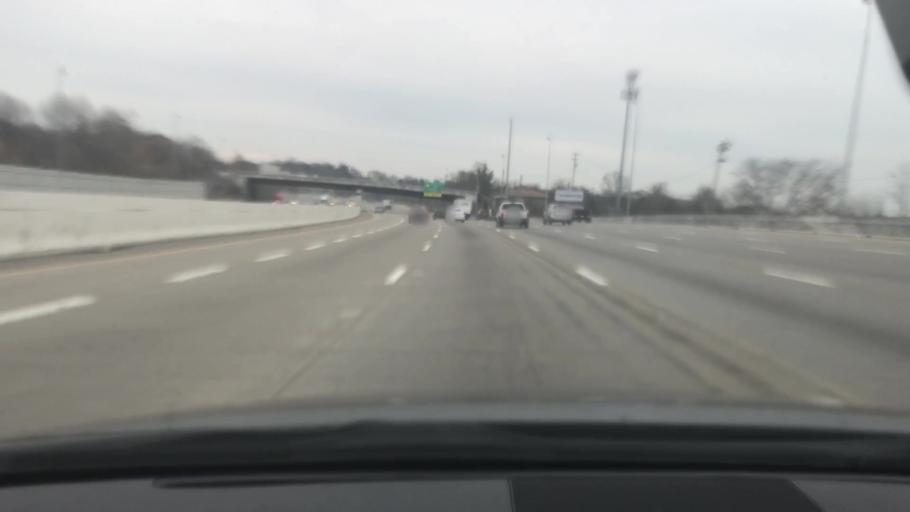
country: US
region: Tennessee
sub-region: Davidson County
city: Goodlettsville
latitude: 36.2479
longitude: -86.7429
